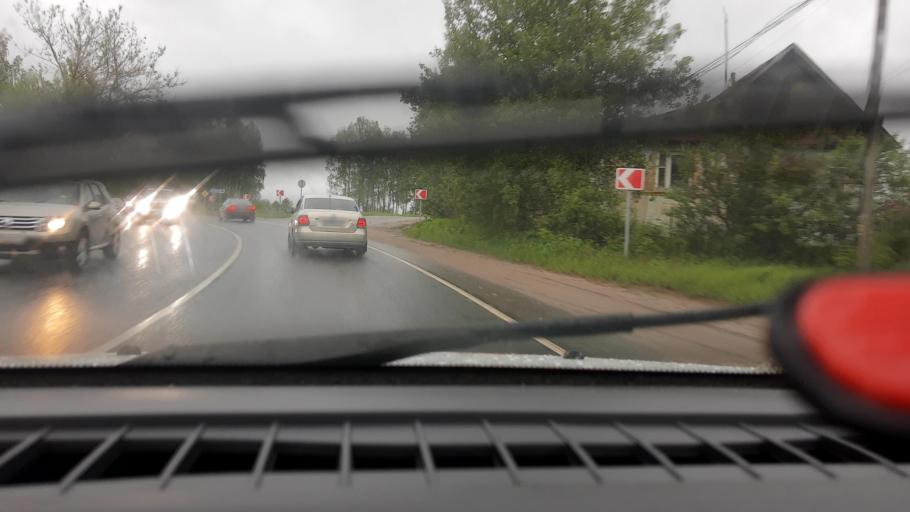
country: RU
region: Nizjnij Novgorod
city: Linda
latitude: 56.6172
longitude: 44.0689
